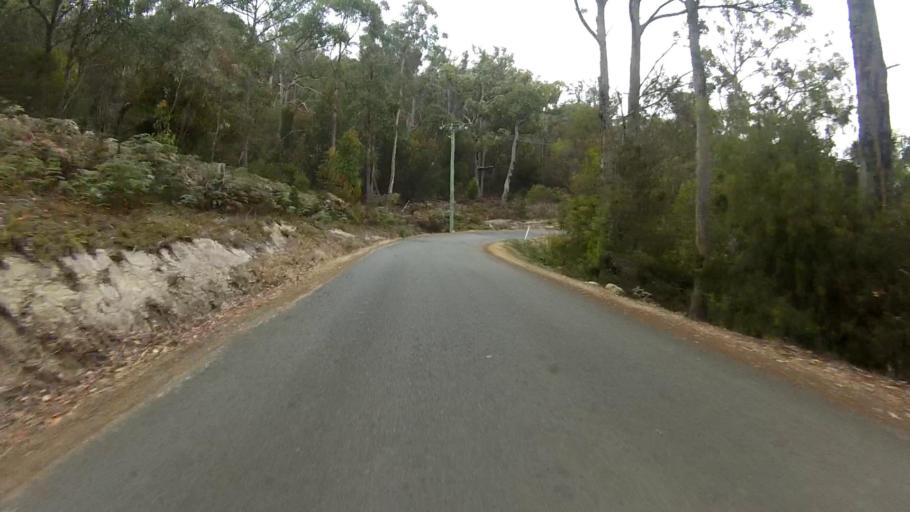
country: AU
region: Tasmania
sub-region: Huon Valley
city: Cygnet
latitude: -43.2169
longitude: 147.0974
